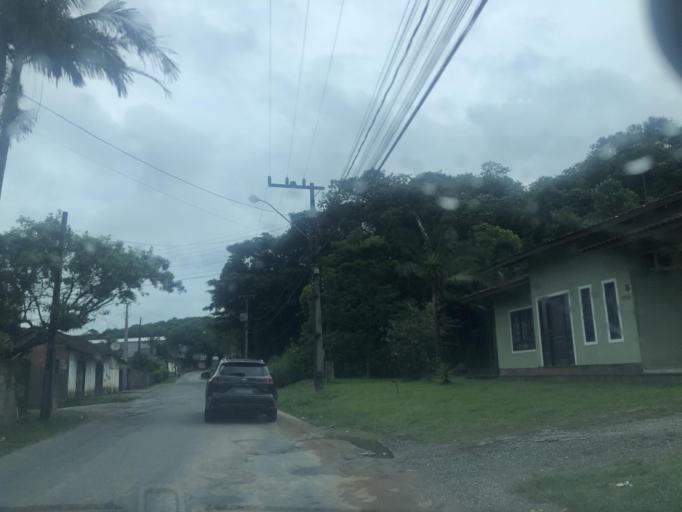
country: BR
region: Santa Catarina
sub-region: Sao Francisco Do Sul
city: Sao Francisco do Sul
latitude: -26.2384
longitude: -48.6156
